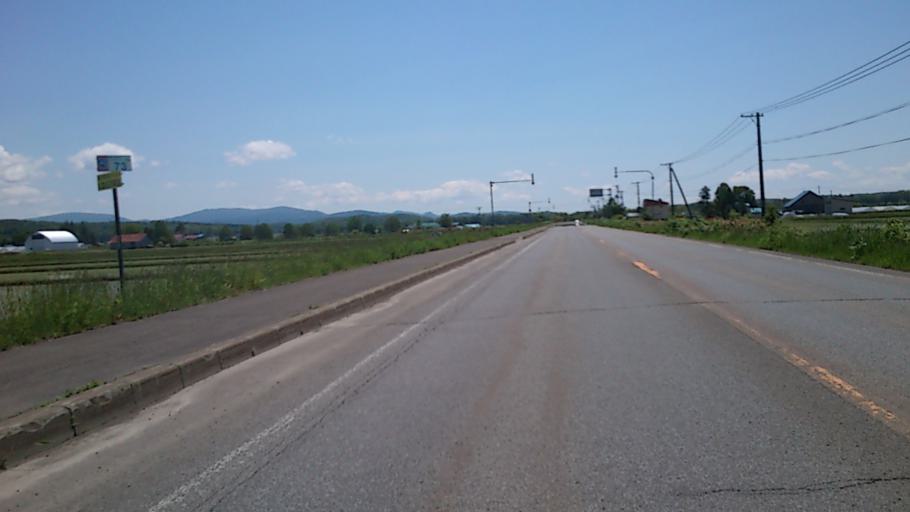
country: JP
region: Hokkaido
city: Nayoro
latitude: 44.3201
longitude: 142.4576
